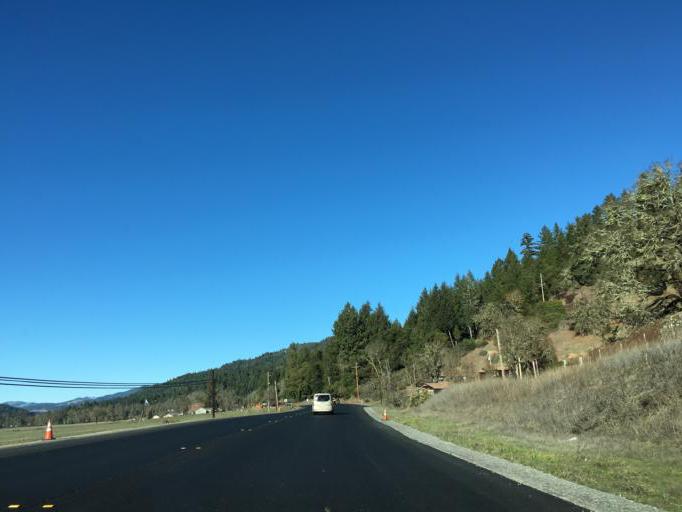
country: US
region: California
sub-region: Mendocino County
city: Laytonville
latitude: 39.6706
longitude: -123.4759
